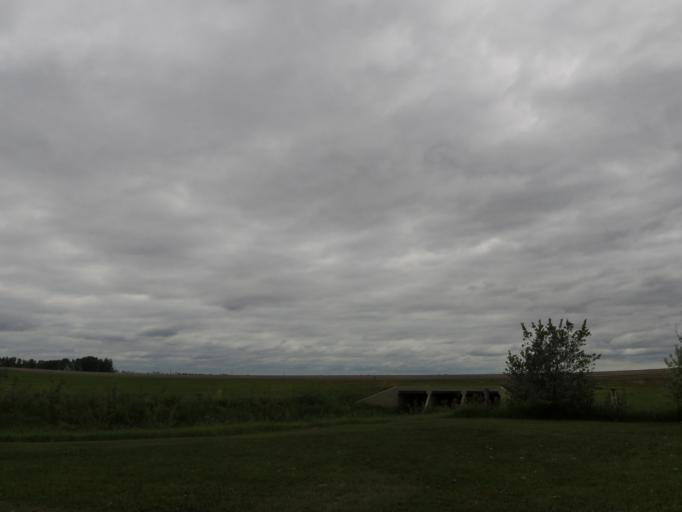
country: US
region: North Dakota
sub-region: Walsh County
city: Grafton
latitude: 48.6200
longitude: -97.4557
